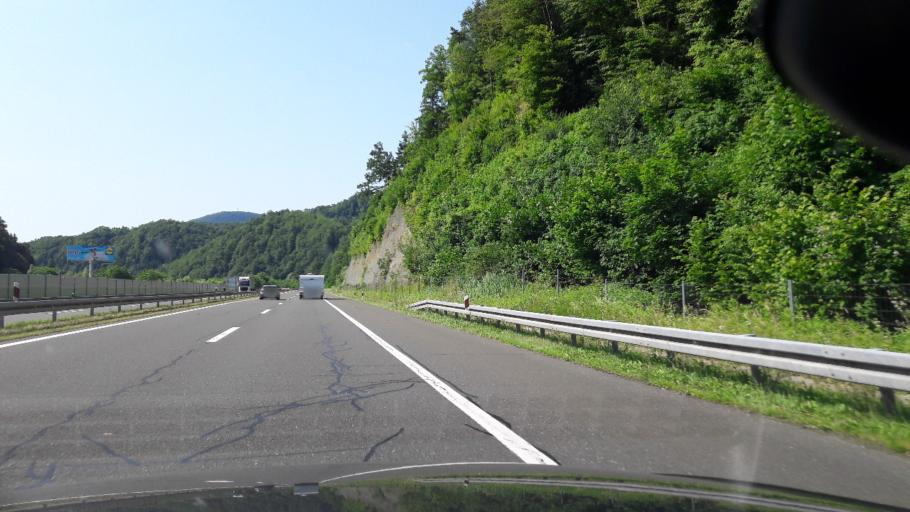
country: SI
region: Zetale
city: Zetale
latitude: 46.2231
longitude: 15.8432
